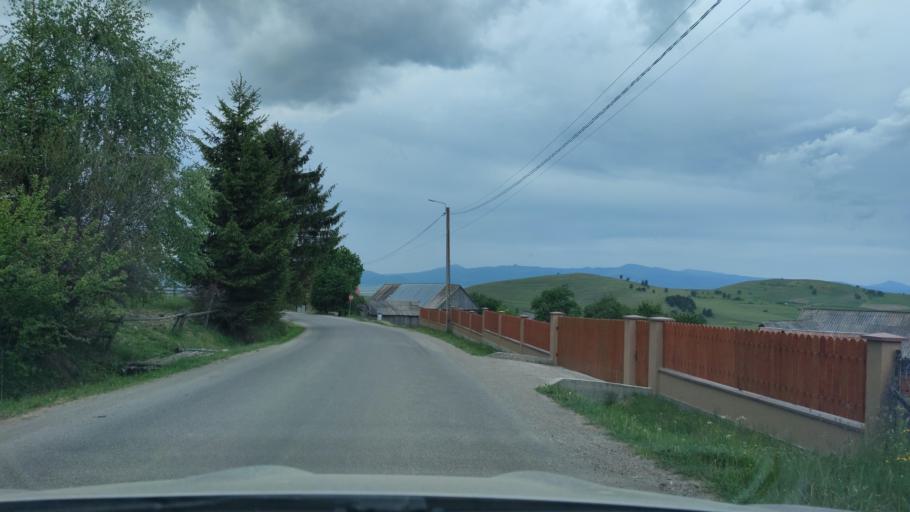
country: RO
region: Harghita
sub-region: Comuna Ditrau
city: Ditrau
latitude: 46.8530
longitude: 25.5062
